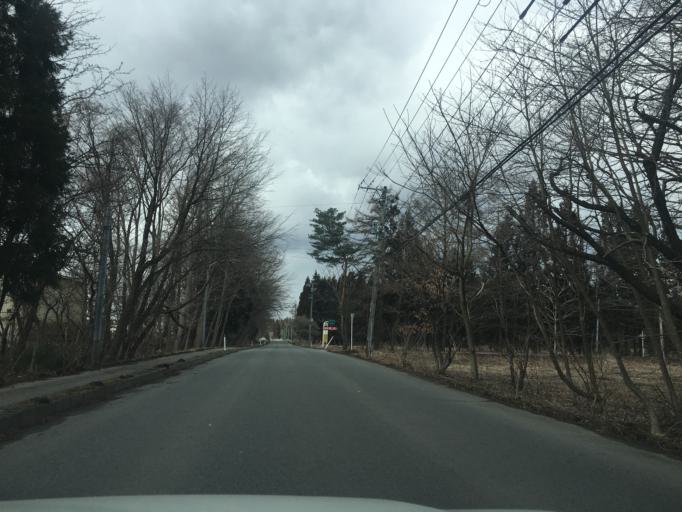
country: JP
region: Akita
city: Takanosu
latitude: 40.1812
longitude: 140.3441
